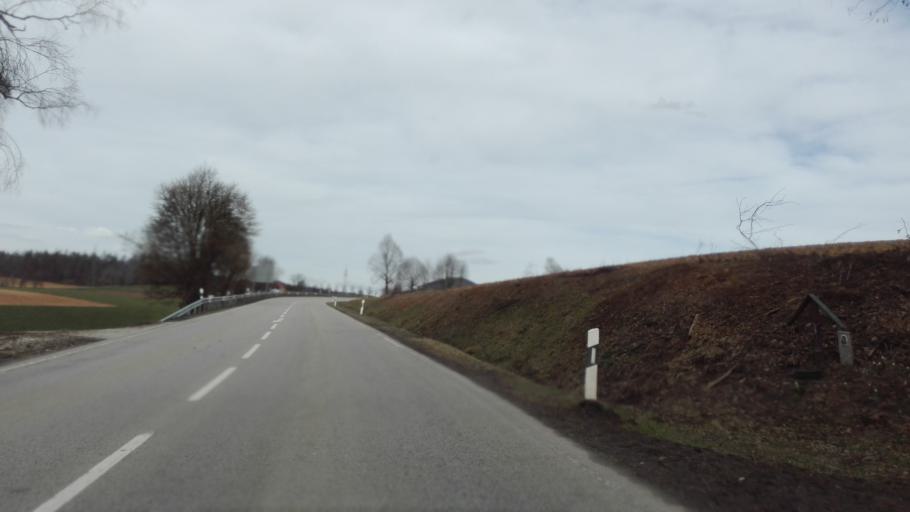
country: DE
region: Bavaria
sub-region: Lower Bavaria
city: Hauzenberg
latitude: 48.6310
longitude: 13.5892
